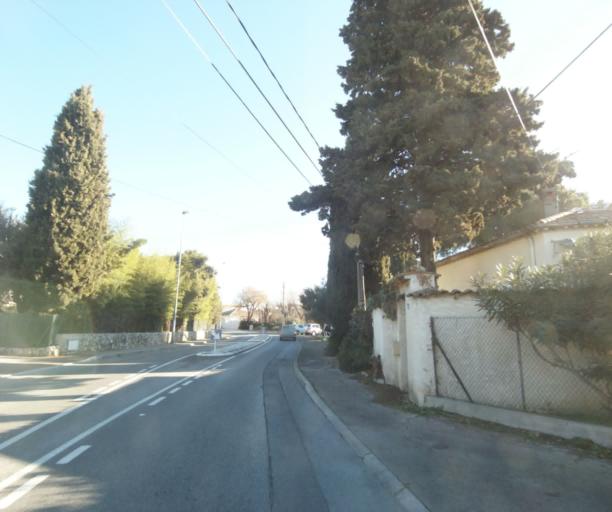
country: FR
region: Provence-Alpes-Cote d'Azur
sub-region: Departement des Alpes-Maritimes
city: Antibes
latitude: 43.5819
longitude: 7.0983
